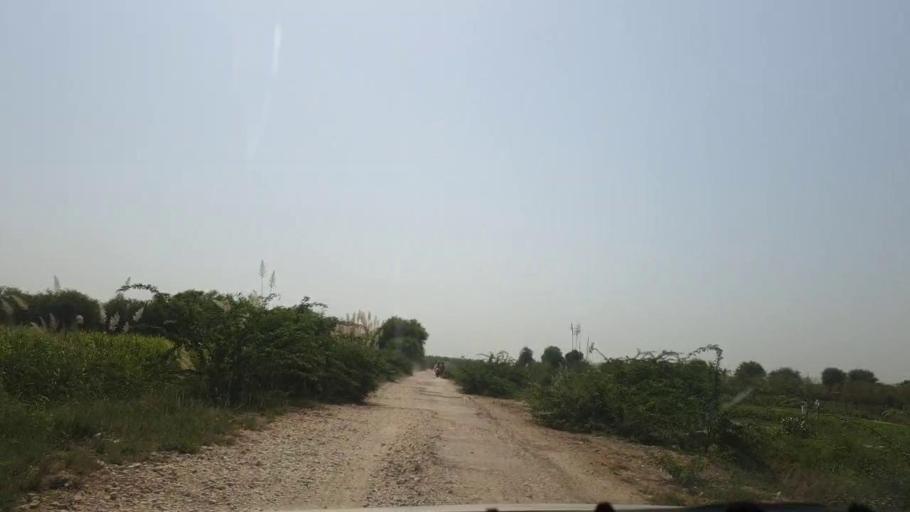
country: PK
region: Sindh
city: Jhol
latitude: 25.8696
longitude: 69.0359
